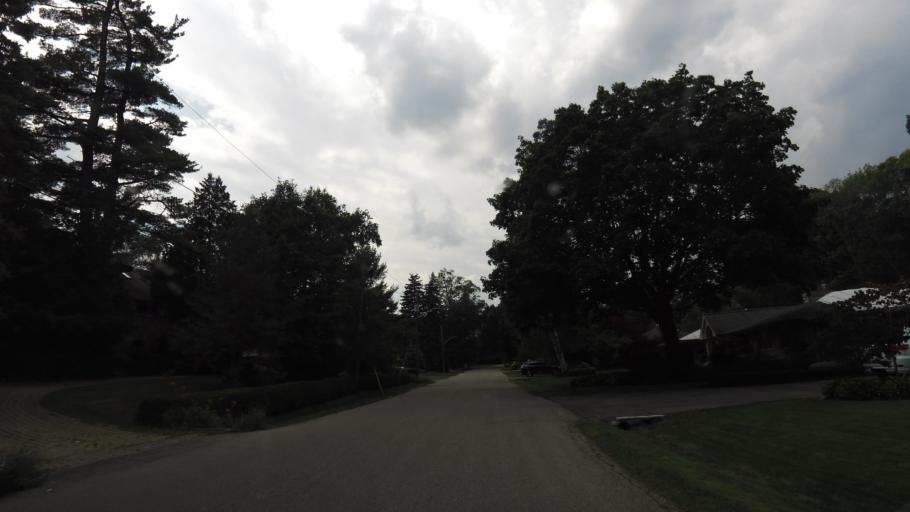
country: CA
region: Ontario
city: Mississauga
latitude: 43.5562
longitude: -79.6054
